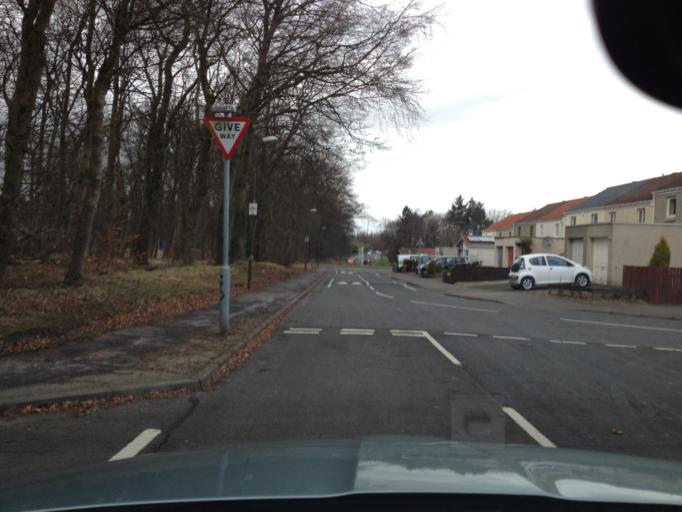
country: GB
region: Scotland
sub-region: West Lothian
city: Livingston
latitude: 55.9009
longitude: -3.5202
